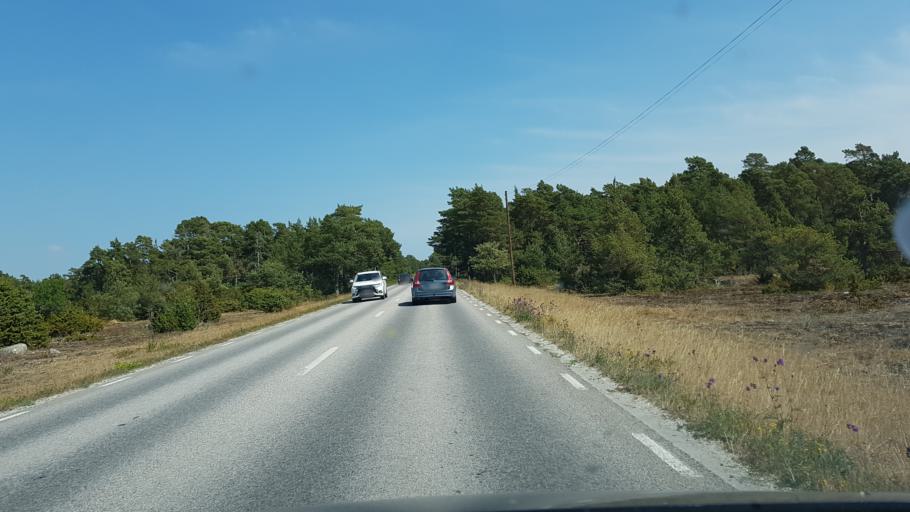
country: SE
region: Gotland
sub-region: Gotland
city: Visby
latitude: 57.6383
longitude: 18.3872
